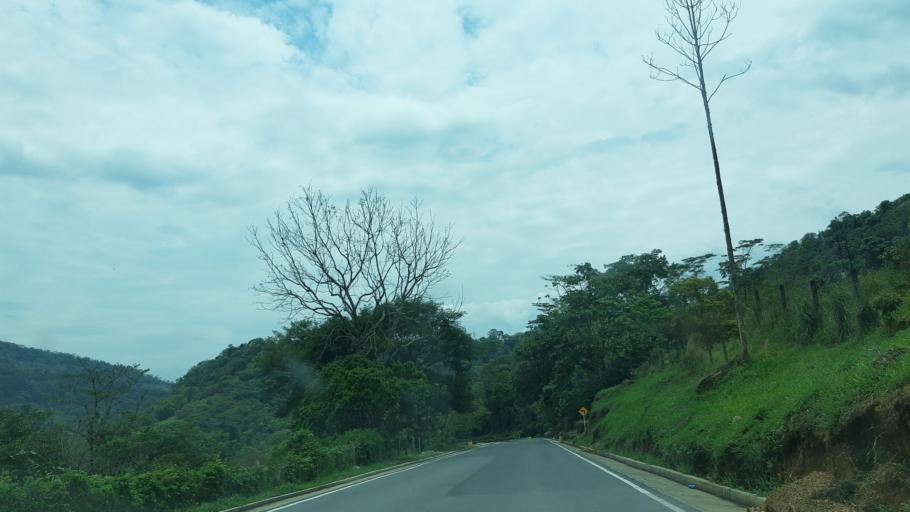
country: CO
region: Casanare
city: Sabanalarga
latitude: 4.8263
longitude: -73.0869
